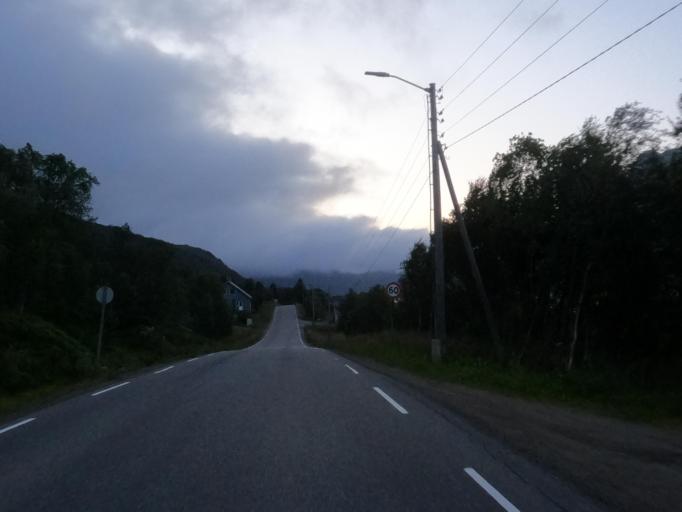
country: NO
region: Nordland
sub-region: Lodingen
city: Lodingen
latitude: 68.5819
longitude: 15.7924
